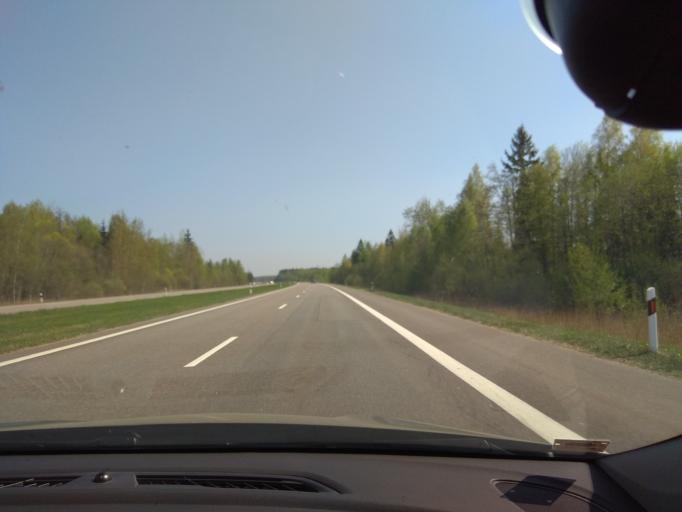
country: LT
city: Ramygala
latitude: 55.5345
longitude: 24.5467
